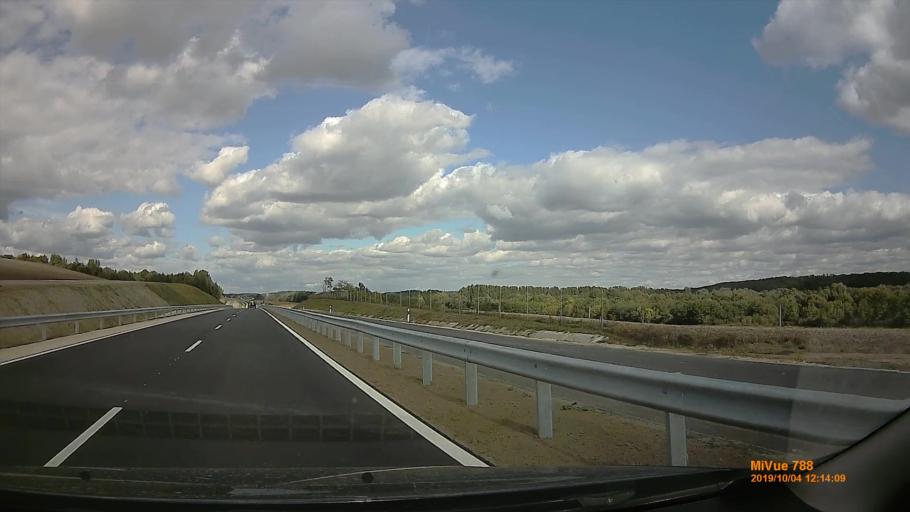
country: HU
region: Somogy
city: Karad
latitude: 46.5320
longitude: 17.8174
